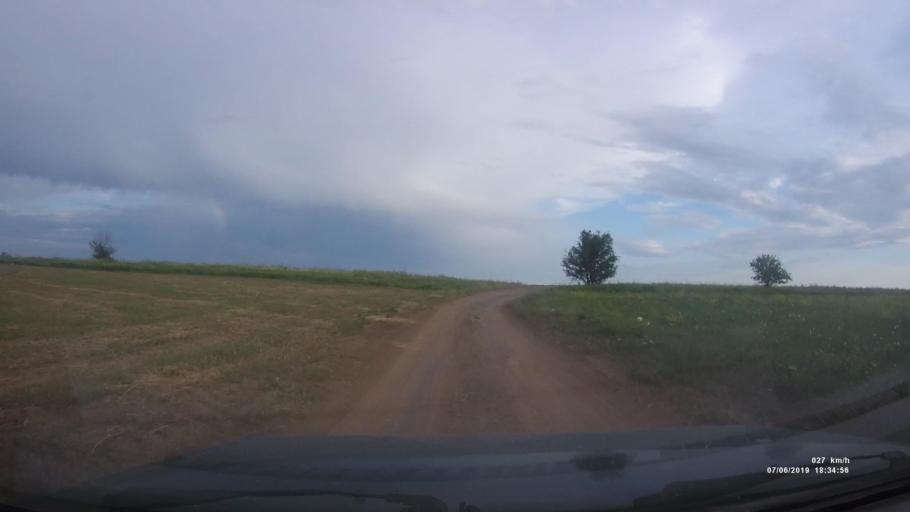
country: RU
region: Rostov
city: Staraya Stanitsa
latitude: 48.2561
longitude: 40.3625
